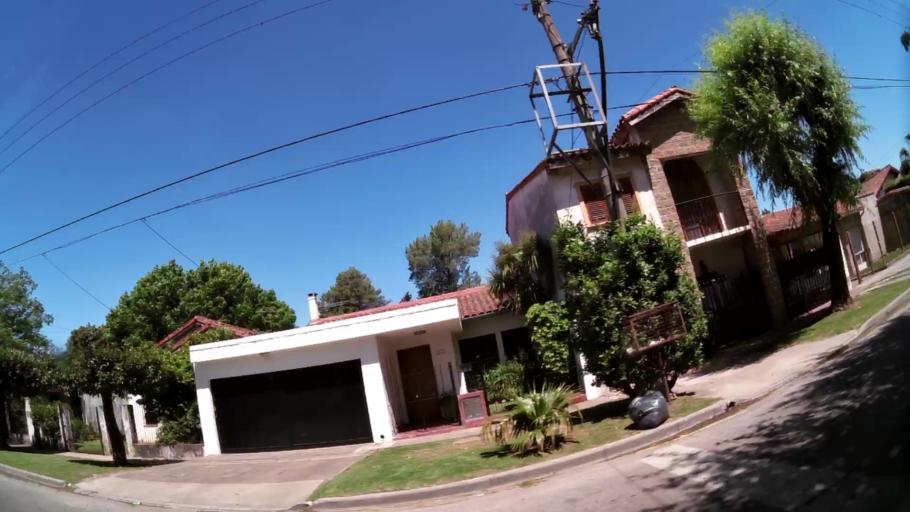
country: AR
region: Buenos Aires
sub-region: Partido de Tigre
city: Tigre
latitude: -34.4892
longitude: -58.6491
